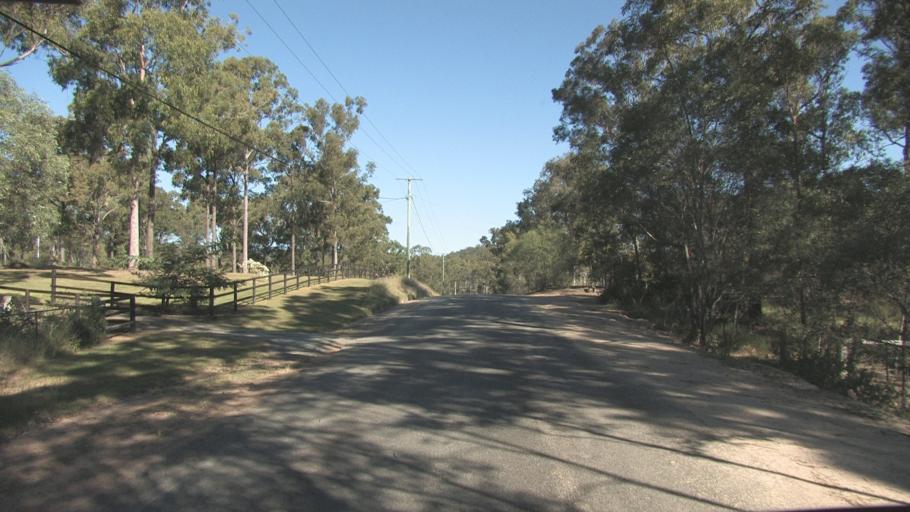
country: AU
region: Queensland
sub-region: Logan
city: Windaroo
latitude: -27.7556
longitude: 153.1513
